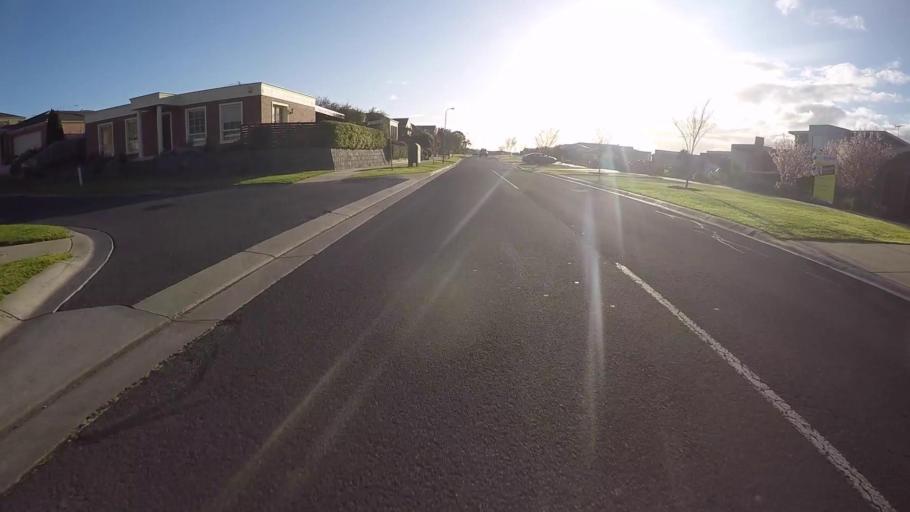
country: AU
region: Victoria
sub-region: Greater Geelong
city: Wandana Heights
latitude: -38.1639
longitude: 144.3072
